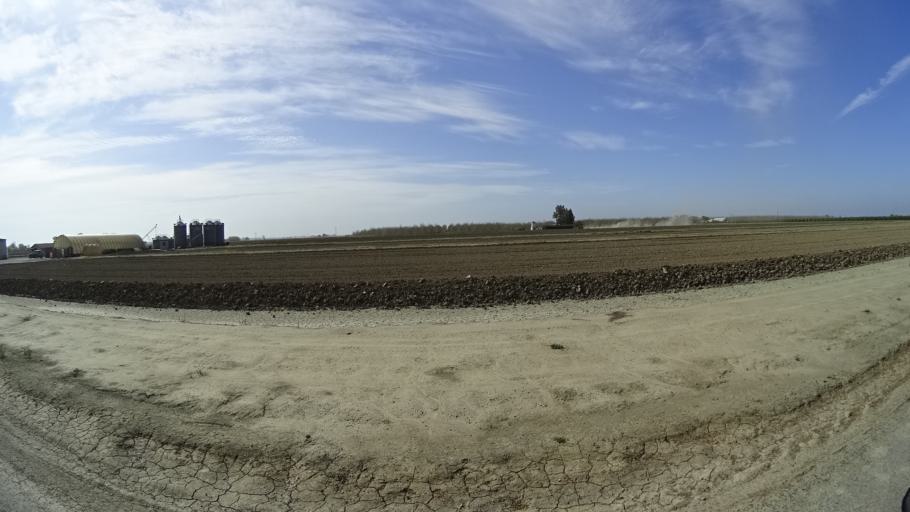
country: US
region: California
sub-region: Glenn County
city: Hamilton City
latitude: 39.6271
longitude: -122.0427
